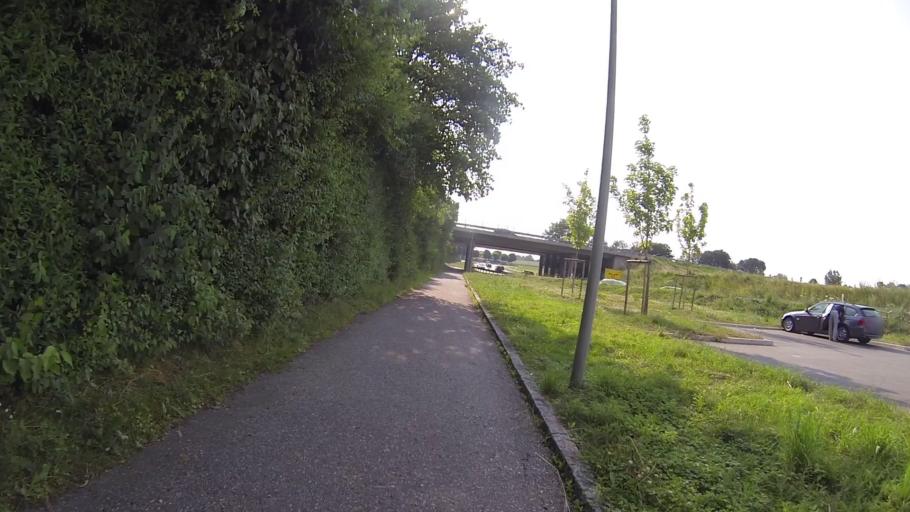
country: DE
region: Baden-Wuerttemberg
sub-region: Tuebingen Region
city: Ulm
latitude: 48.4379
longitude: 9.9773
